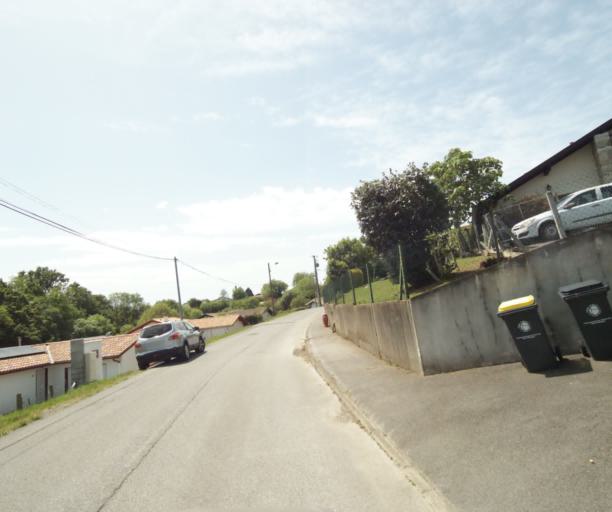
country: FR
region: Aquitaine
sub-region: Departement des Pyrenees-Atlantiques
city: Mouguerre
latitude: 43.4584
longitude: -1.4307
